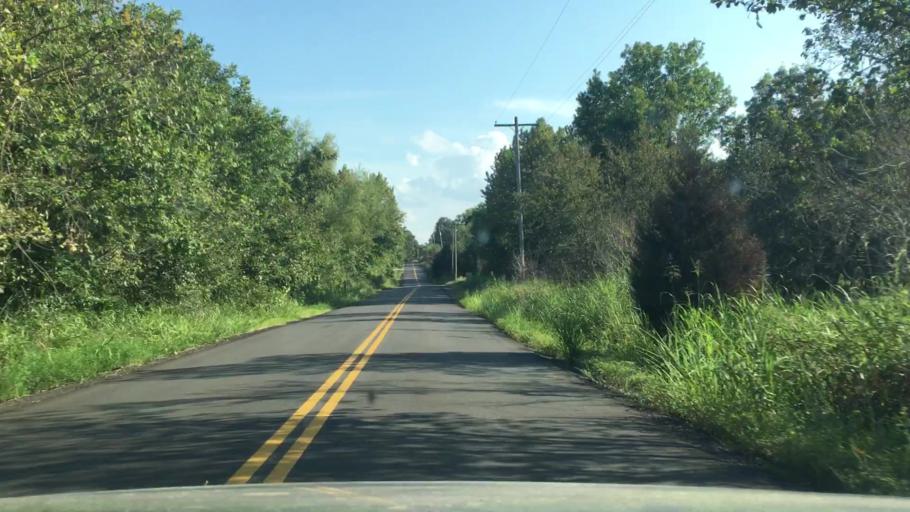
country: US
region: Oklahoma
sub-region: Muskogee County
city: Fort Gibson
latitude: 35.6464
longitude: -95.2161
